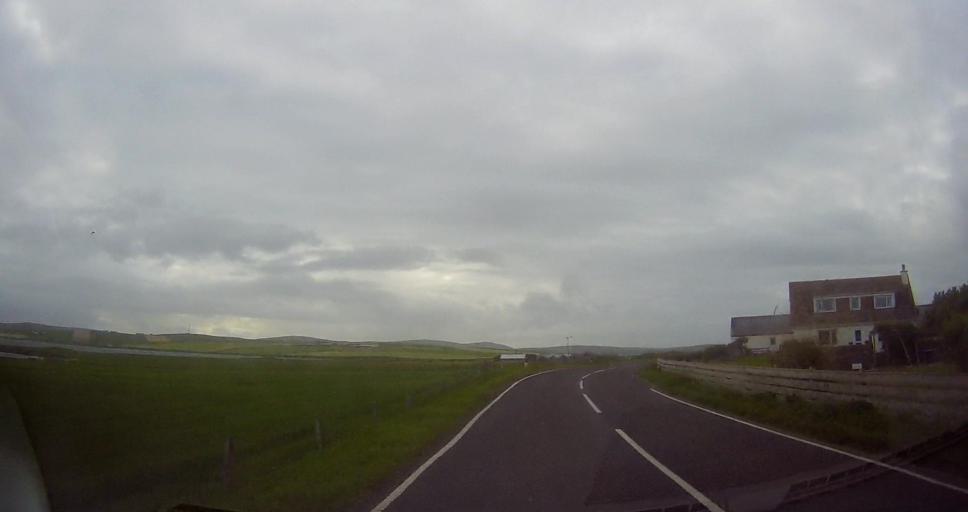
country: GB
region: Scotland
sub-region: Orkney Islands
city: Stromness
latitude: 58.9724
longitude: -3.2367
